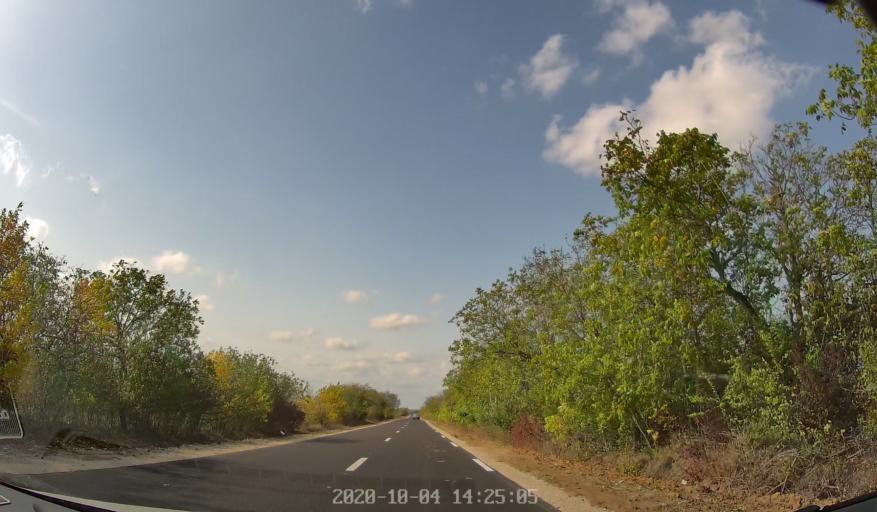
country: MD
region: Rezina
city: Saharna
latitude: 47.6179
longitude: 28.9048
